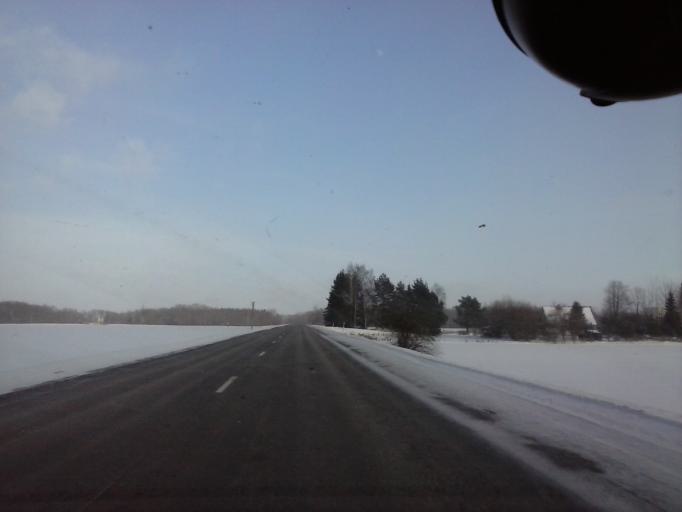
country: EE
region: Tartu
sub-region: Puhja vald
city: Puhja
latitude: 58.3284
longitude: 26.2841
